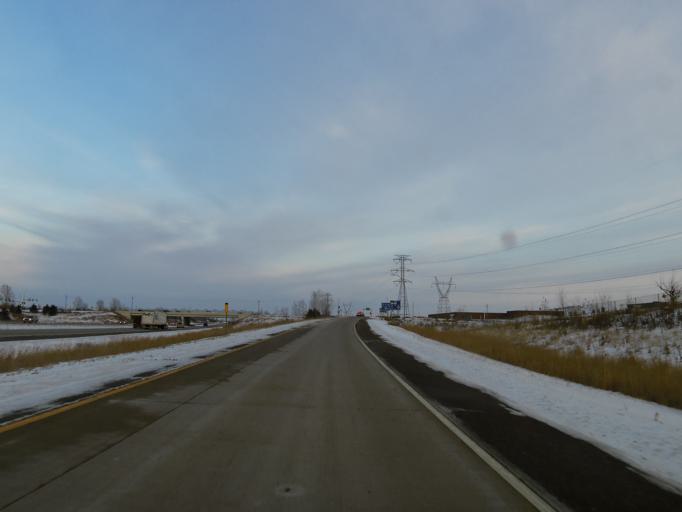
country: US
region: Minnesota
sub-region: Scott County
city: Shakopee
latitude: 44.7773
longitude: -93.5093
